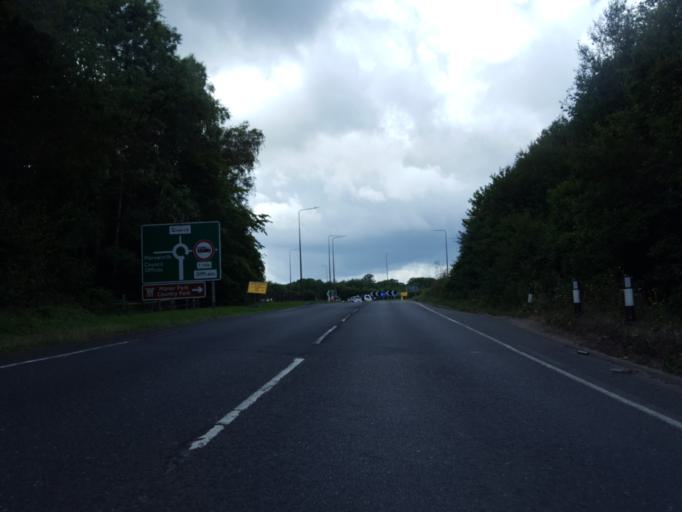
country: GB
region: England
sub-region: Kent
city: Kings Hill
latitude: 51.2798
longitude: 0.3966
